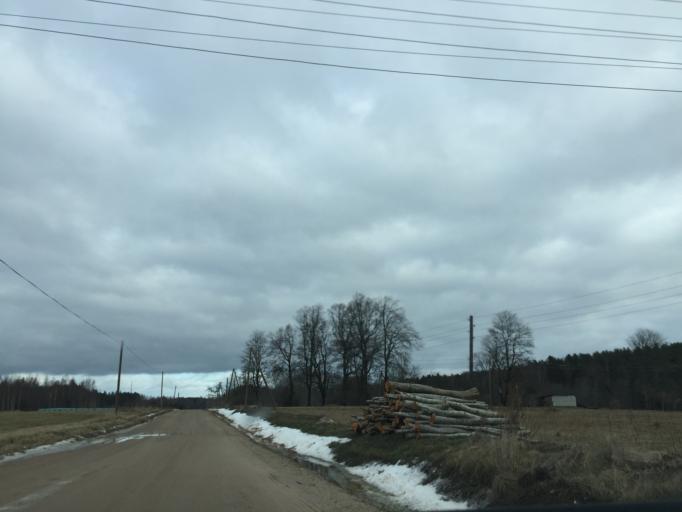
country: LV
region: Salacgrivas
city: Ainazi
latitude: 57.8510
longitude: 24.4878
